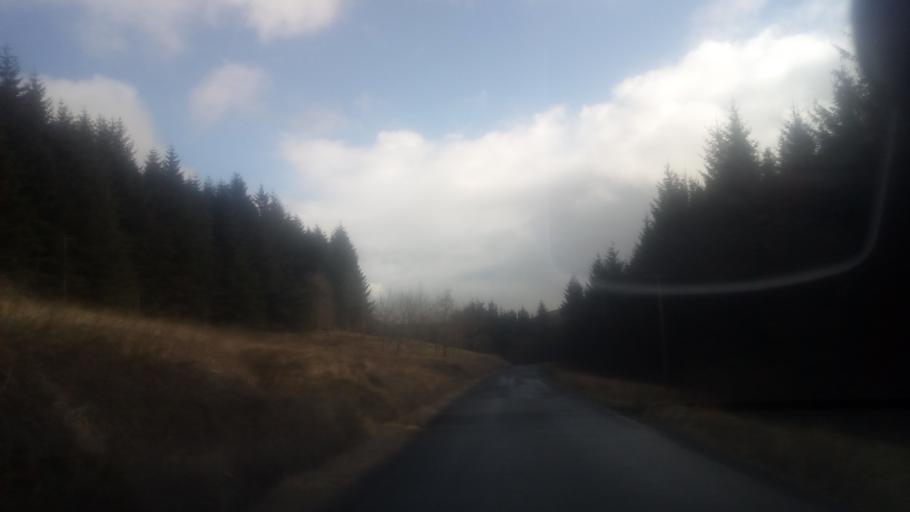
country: GB
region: Scotland
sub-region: The Scottish Borders
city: Innerleithen
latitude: 55.4679
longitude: -3.1384
